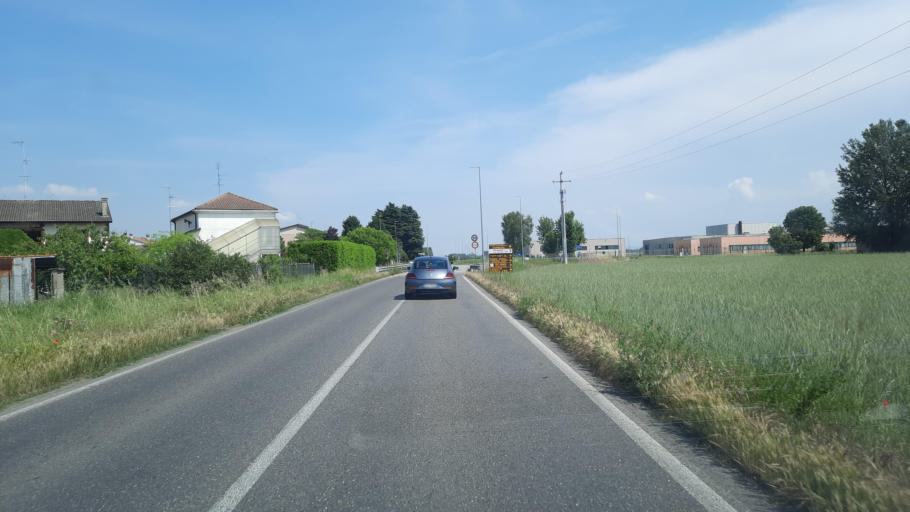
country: IT
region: Lombardy
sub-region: Provincia di Pavia
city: Carbonara al Ticino
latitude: 45.1627
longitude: 9.0639
